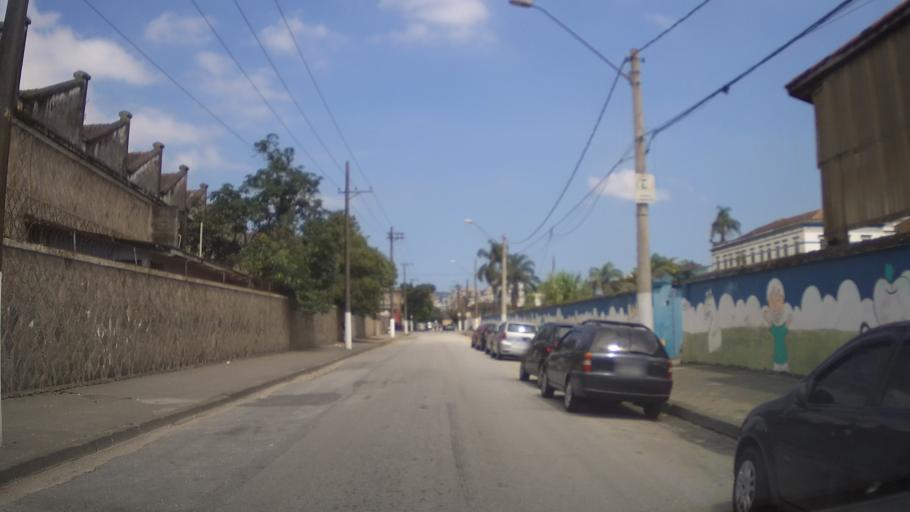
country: BR
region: Sao Paulo
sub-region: Santos
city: Santos
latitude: -23.9553
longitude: -46.3120
